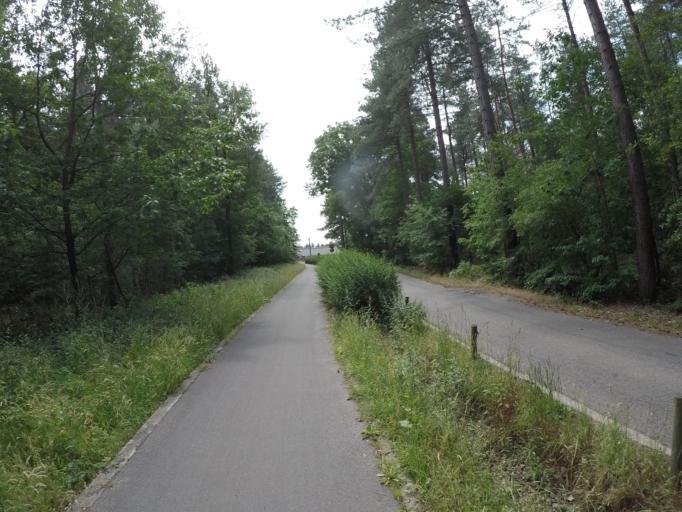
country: BE
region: Flanders
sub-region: Provincie Antwerpen
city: Essen
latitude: 51.4680
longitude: 4.5304
